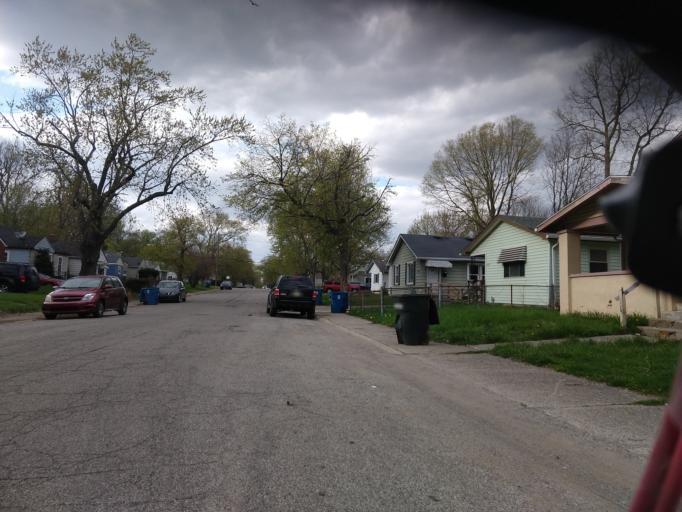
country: US
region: Indiana
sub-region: Marion County
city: Broad Ripple
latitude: 39.8355
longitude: -86.1289
